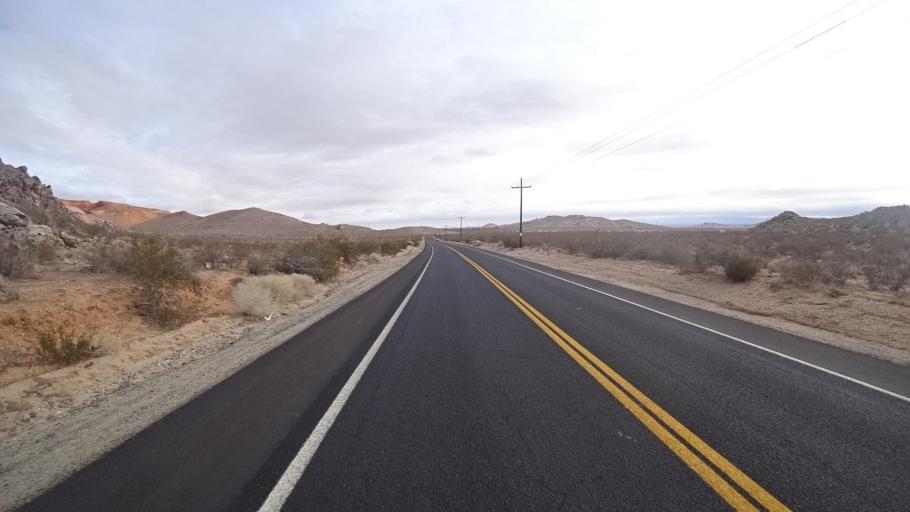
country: US
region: California
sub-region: Kern County
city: Rosamond
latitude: 34.9500
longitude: -118.2855
